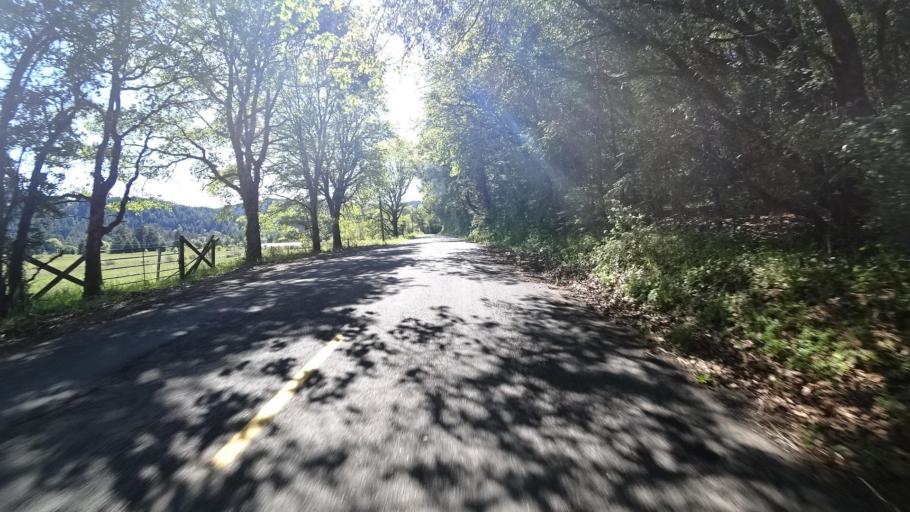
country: US
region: California
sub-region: Humboldt County
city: Rio Dell
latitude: 40.2380
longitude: -124.1610
